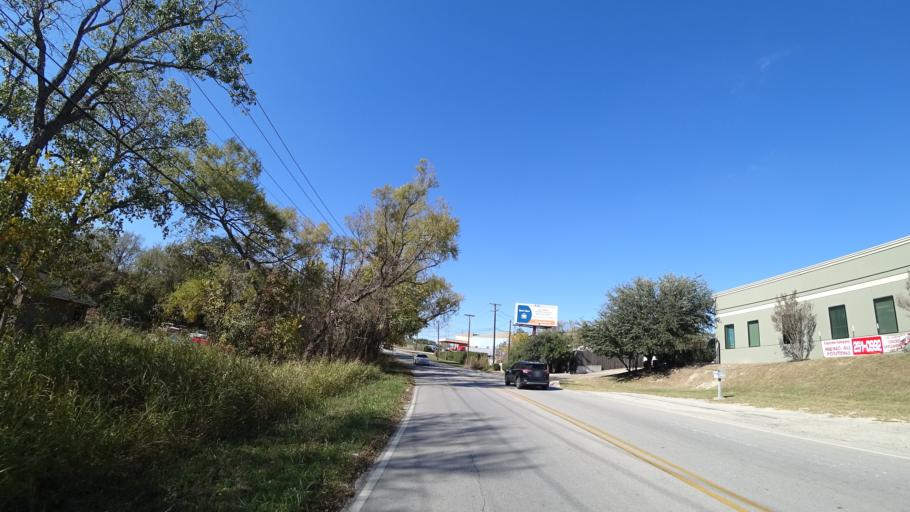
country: US
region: Texas
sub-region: Travis County
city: Wells Branch
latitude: 30.4346
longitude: -97.6862
